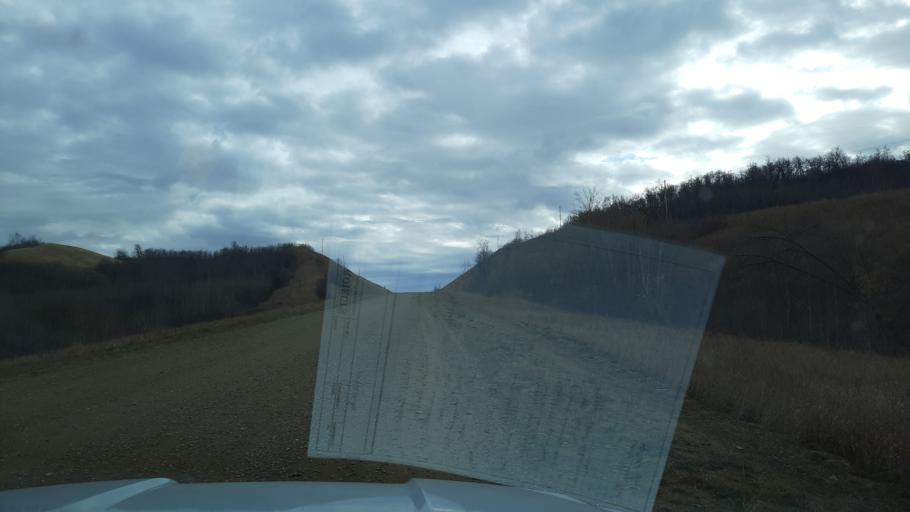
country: CA
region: Saskatchewan
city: Pilot Butte
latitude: 50.7686
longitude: -104.2791
